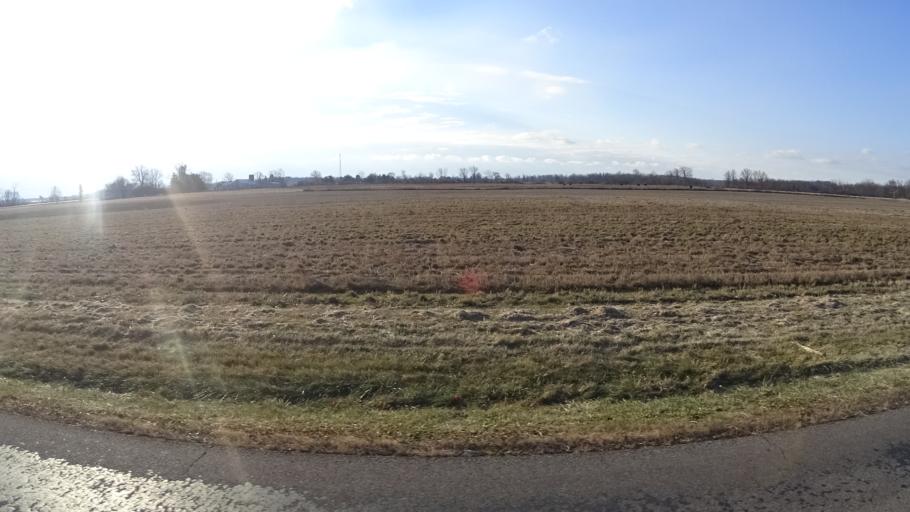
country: US
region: Ohio
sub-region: Lorain County
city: Oberlin
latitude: 41.2508
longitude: -82.2209
